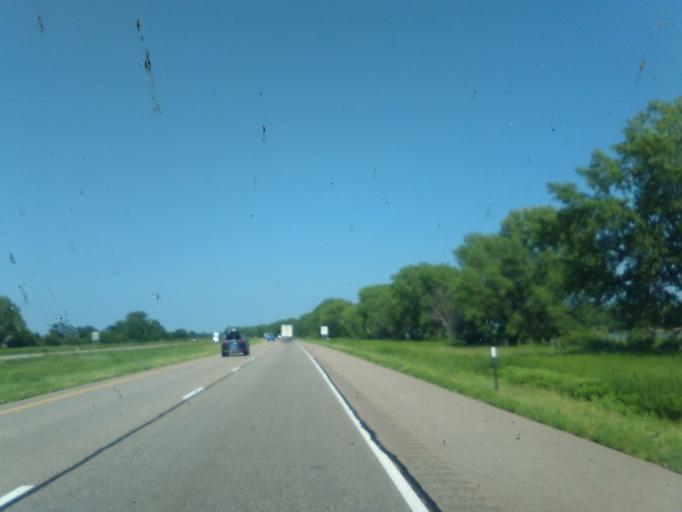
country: US
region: Nebraska
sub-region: Buffalo County
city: Shelton
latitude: 40.7250
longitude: -98.6784
